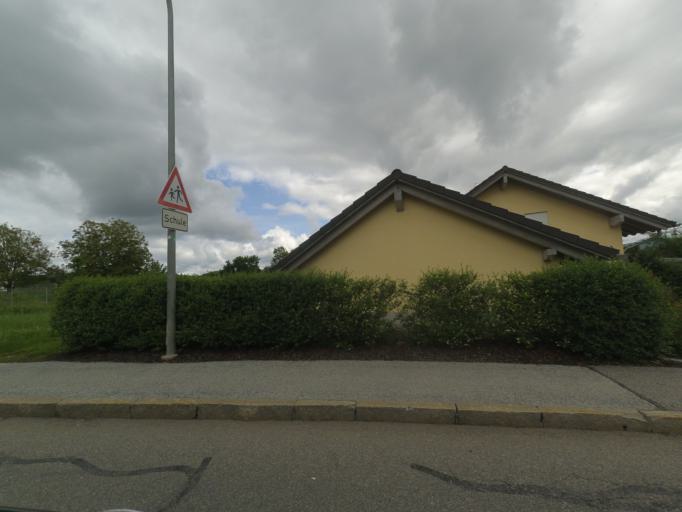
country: DE
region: Bavaria
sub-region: Lower Bavaria
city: Regen
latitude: 48.9734
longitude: 13.1210
